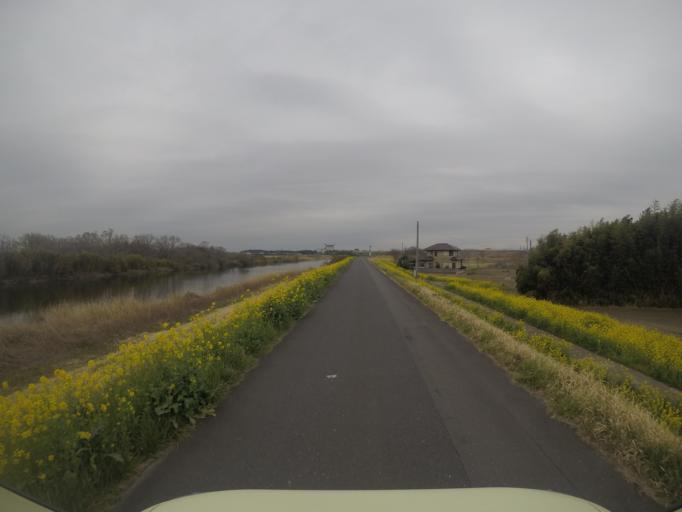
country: JP
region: Ibaraki
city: Ishige
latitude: 36.0843
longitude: 139.9998
